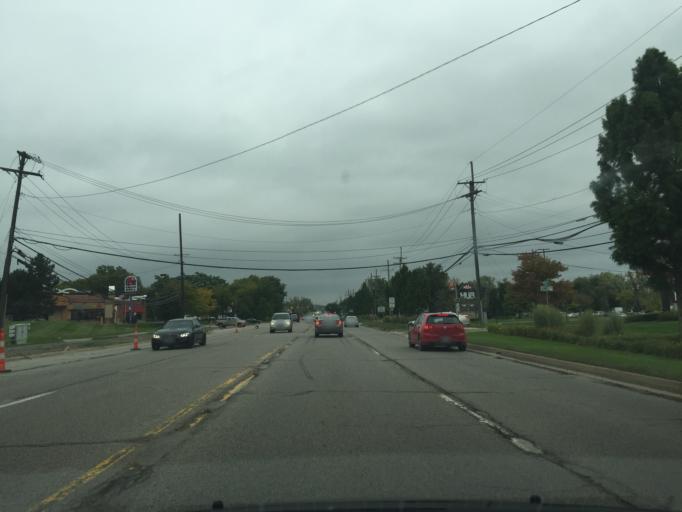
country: US
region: Michigan
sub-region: Oakland County
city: Auburn Hills
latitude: 42.6587
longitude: -83.2457
